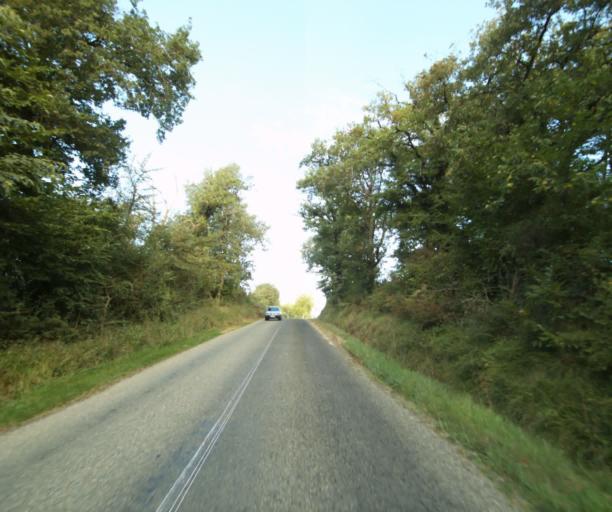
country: FR
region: Midi-Pyrenees
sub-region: Departement du Gers
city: Eauze
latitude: 43.8999
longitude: 0.0316
